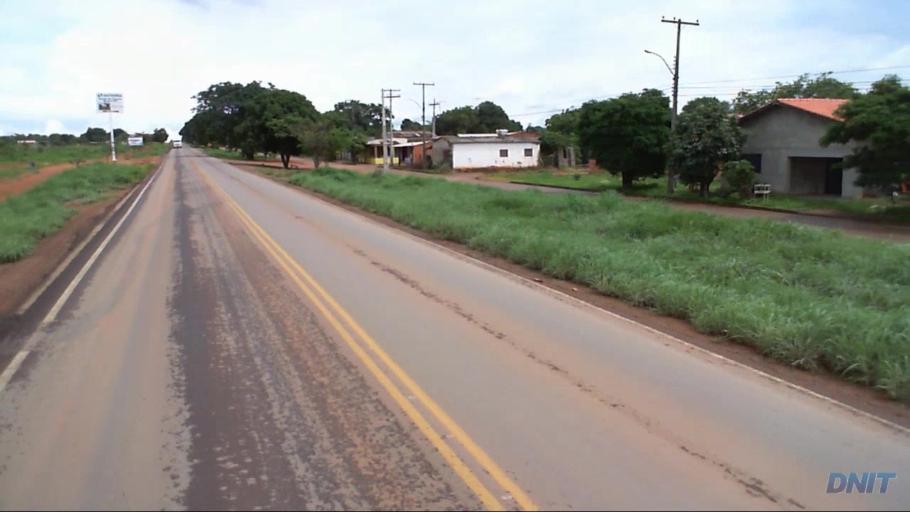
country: BR
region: Goias
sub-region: Padre Bernardo
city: Padre Bernardo
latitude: -15.2613
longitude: -48.2654
